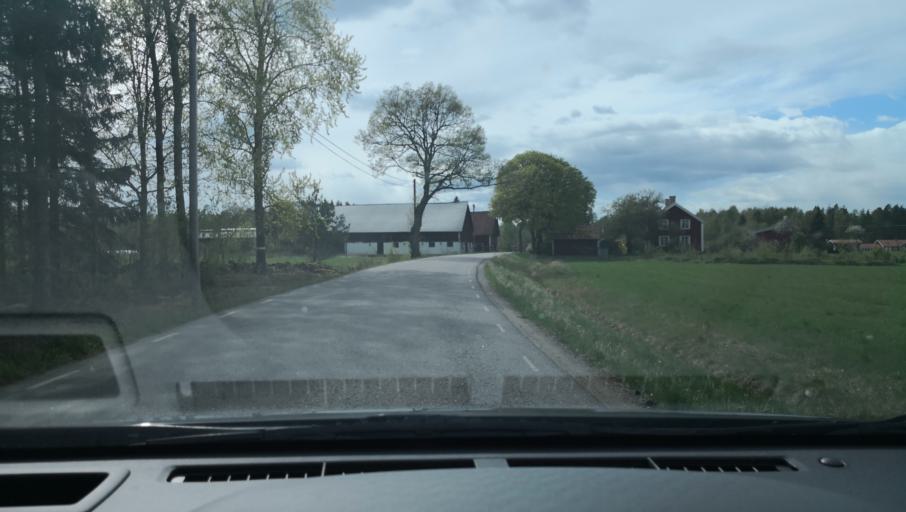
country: SE
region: OErebro
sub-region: Kumla Kommun
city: Hallabrottet
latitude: 59.1631
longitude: 15.2470
